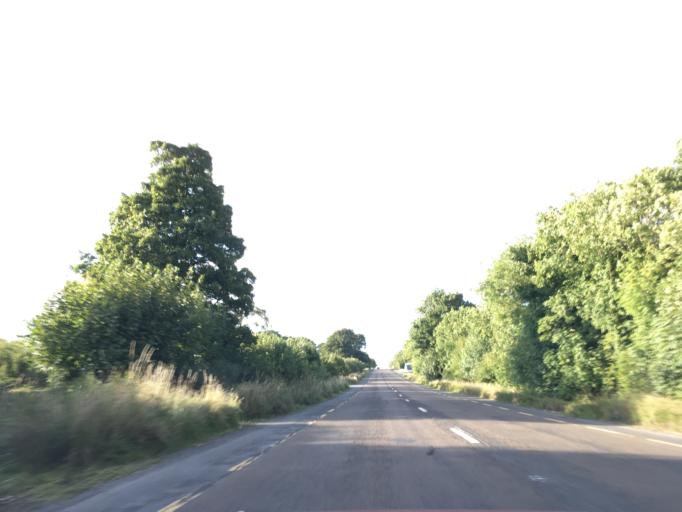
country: IE
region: Munster
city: Cashel
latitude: 52.4858
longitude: -7.8912
